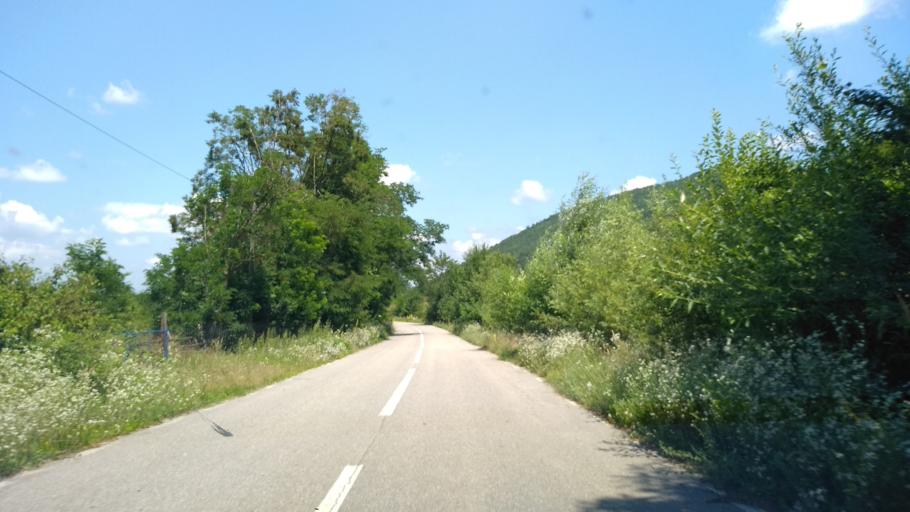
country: RO
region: Hunedoara
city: Berca
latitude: 45.6080
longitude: 23.0224
